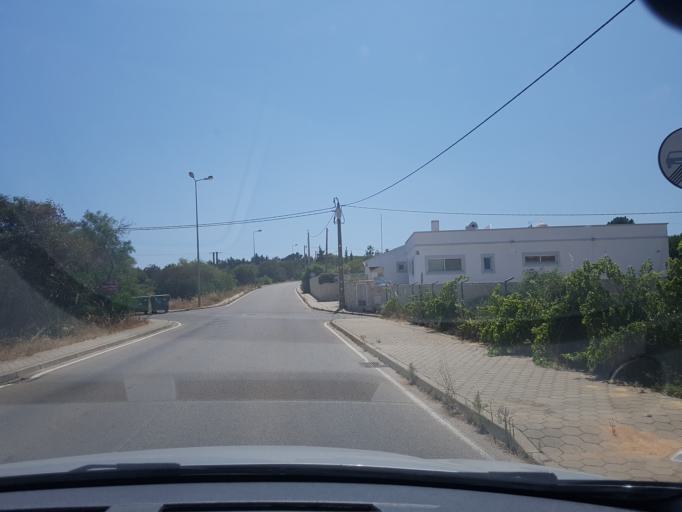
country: PT
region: Faro
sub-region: Lagoa
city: Carvoeiro
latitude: 37.1051
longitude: -8.4381
